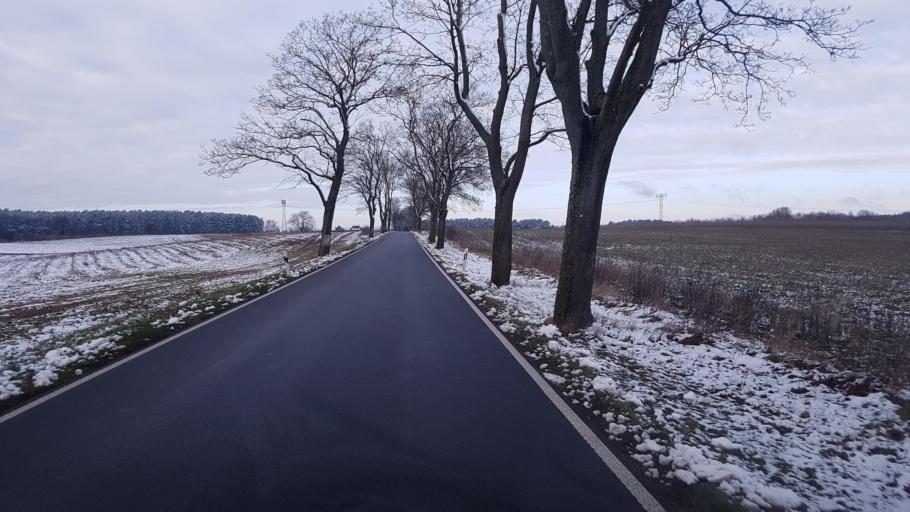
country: DE
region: Brandenburg
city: Strausberg
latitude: 52.5607
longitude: 13.9058
